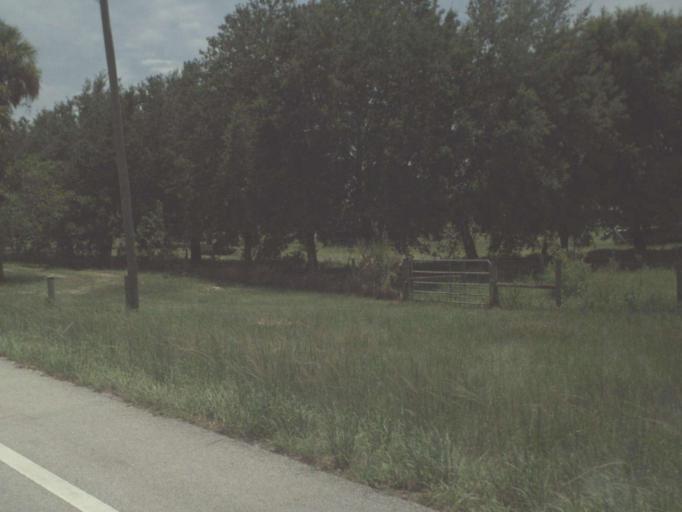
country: US
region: Florida
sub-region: Okeechobee County
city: Taylor Creek
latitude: 27.1104
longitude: -80.6636
